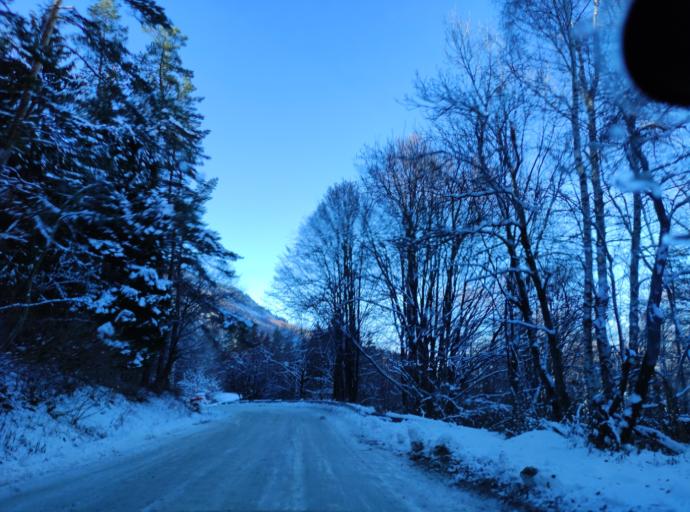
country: BG
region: Sofia-Capital
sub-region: Stolichna Obshtina
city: Sofia
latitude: 42.6041
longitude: 23.3014
